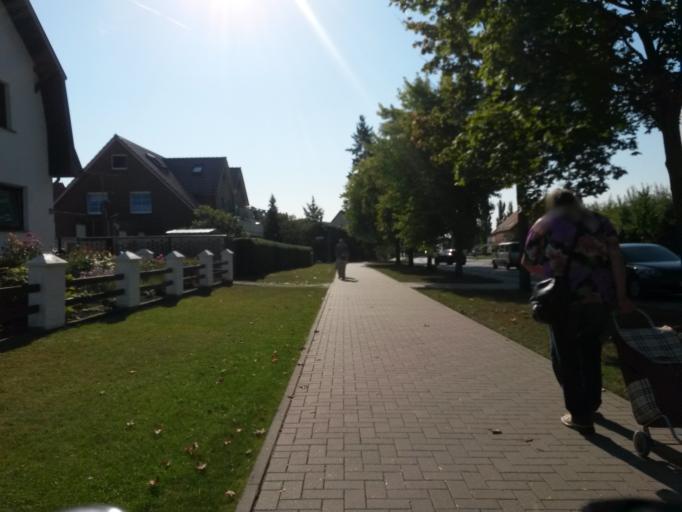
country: DE
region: Brandenburg
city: Templin
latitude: 53.1270
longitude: 13.4915
